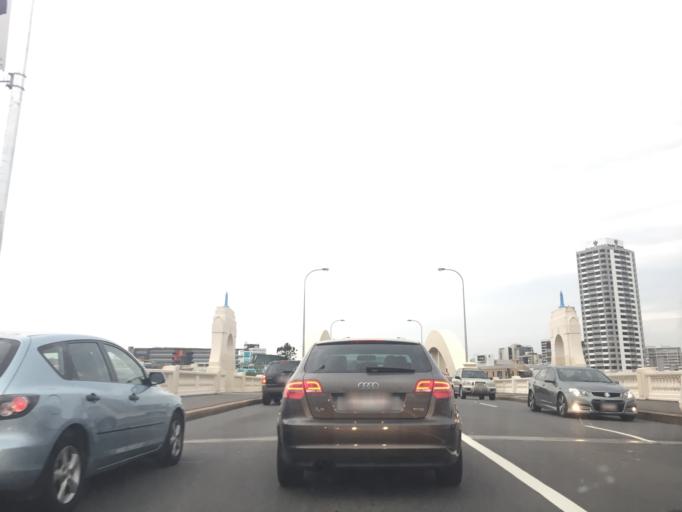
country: AU
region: Queensland
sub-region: Brisbane
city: Spring Hill
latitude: -27.4698
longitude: 153.0158
